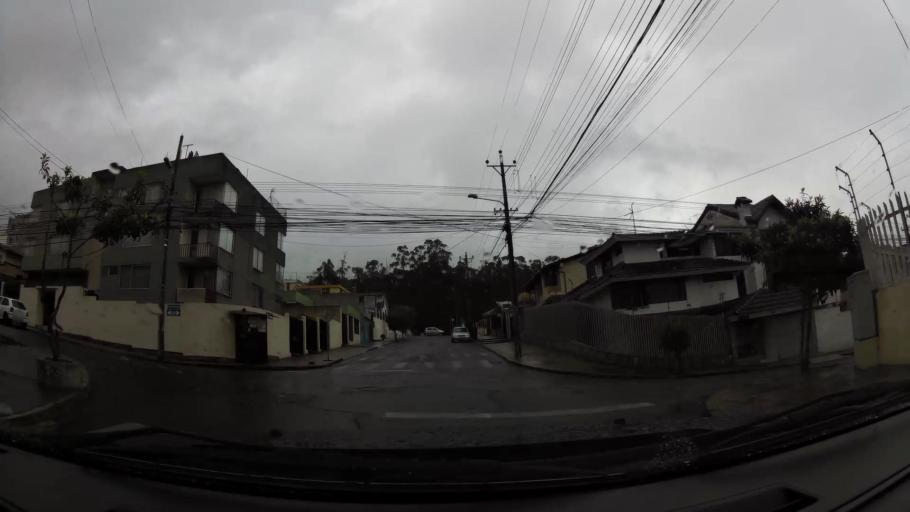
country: EC
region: Pichincha
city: Quito
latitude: -0.1096
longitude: -78.4998
